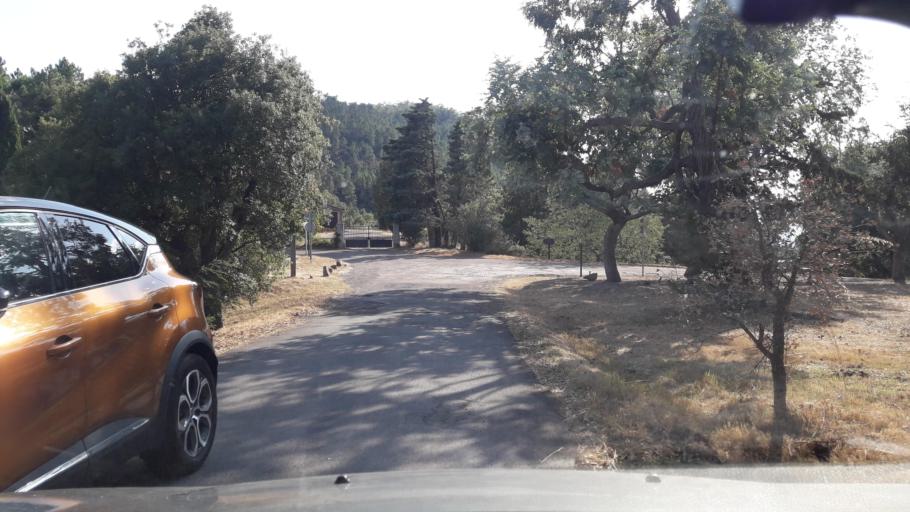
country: FR
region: Provence-Alpes-Cote d'Azur
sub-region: Departement du Var
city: Saint-Raphael
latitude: 43.4959
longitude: 6.8021
